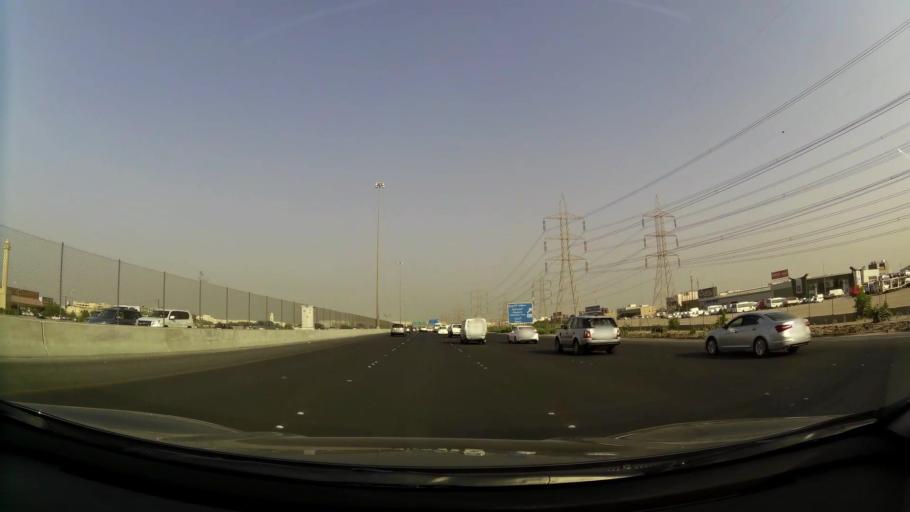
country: KW
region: Al Asimah
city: Ar Rabiyah
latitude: 29.2995
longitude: 47.9182
